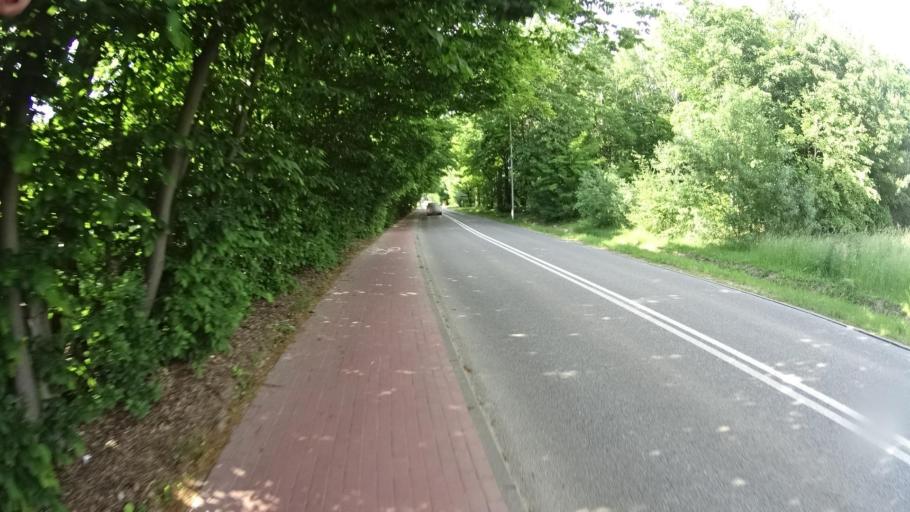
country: PL
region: Masovian Voivodeship
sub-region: Powiat pruszkowski
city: Granica
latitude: 52.1136
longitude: 20.7984
